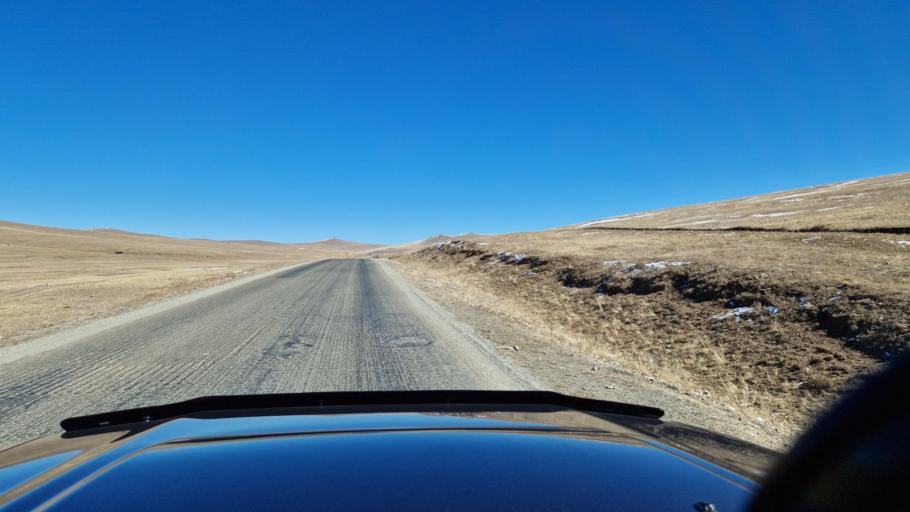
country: MN
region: Hentiy
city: Modot
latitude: 47.7896
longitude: 108.6769
